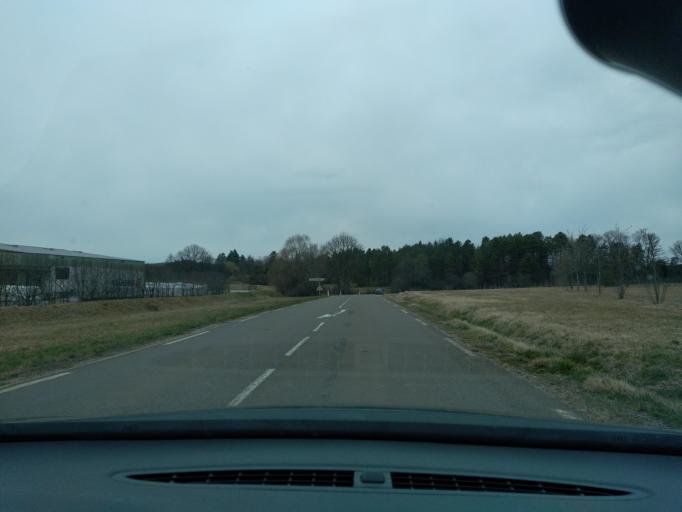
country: FR
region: Franche-Comte
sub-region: Departement du Jura
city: Arinthod
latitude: 46.4034
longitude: 5.5635
